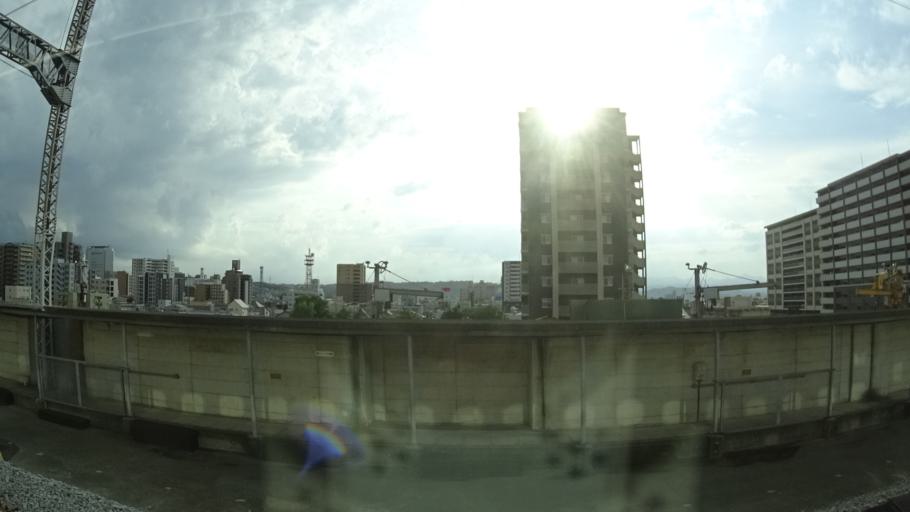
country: JP
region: Gunma
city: Takasaki
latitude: 36.3298
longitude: 139.0121
